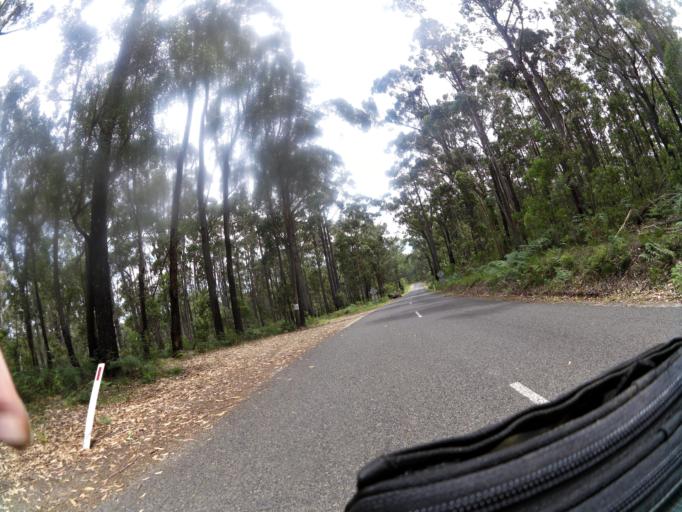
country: AU
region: Victoria
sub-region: East Gippsland
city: Lakes Entrance
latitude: -37.6967
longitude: 148.7421
